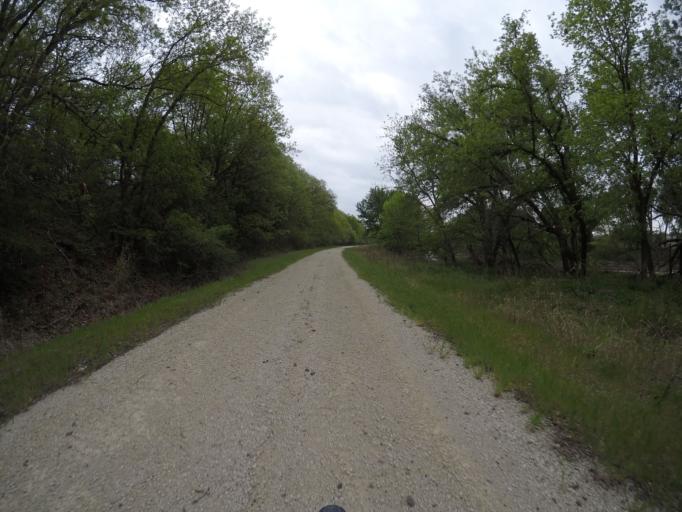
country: US
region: Nebraska
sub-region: Gage County
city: Wymore
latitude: 40.1143
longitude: -96.6277
